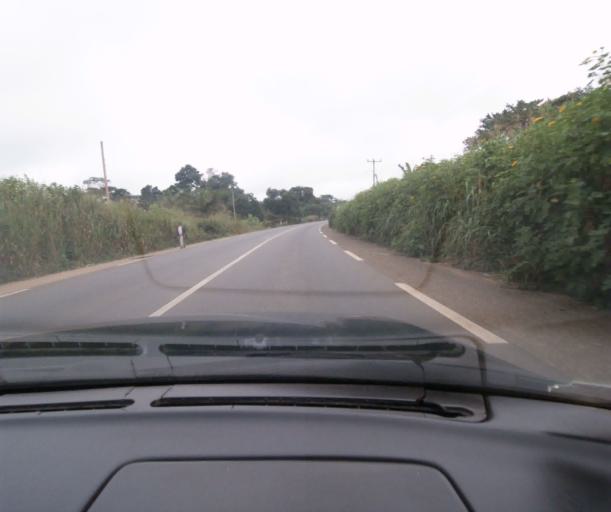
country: CM
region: Centre
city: Obala
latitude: 4.1893
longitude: 11.4545
